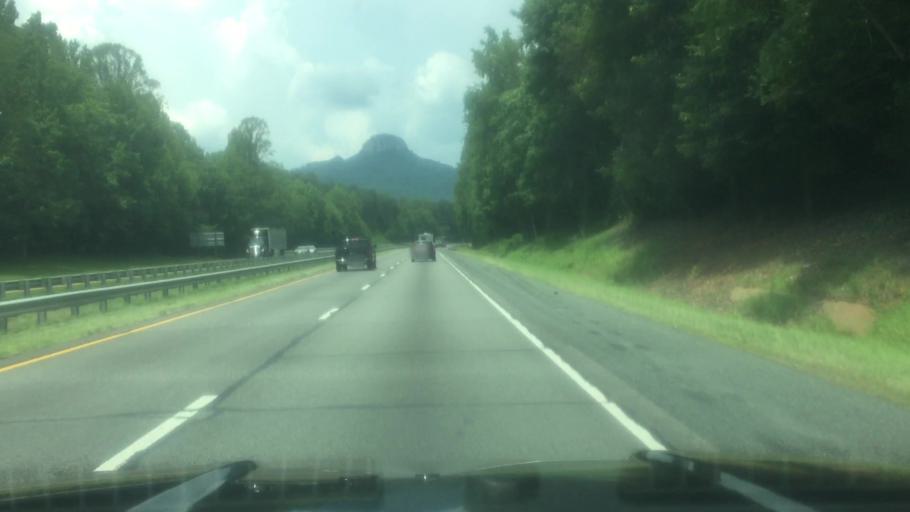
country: US
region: North Carolina
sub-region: Surry County
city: Pilot Mountain
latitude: 36.3217
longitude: -80.4450
